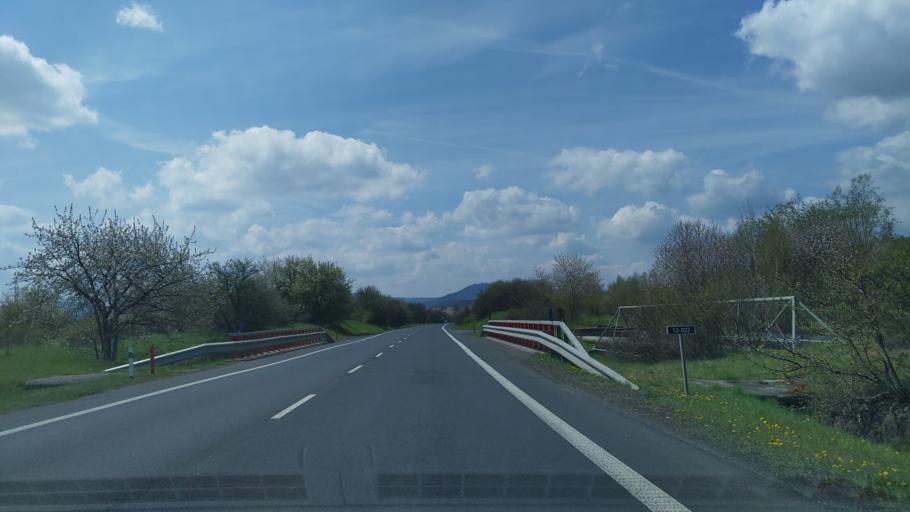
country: CZ
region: Ustecky
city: Kadan
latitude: 50.4096
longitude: 13.2436
